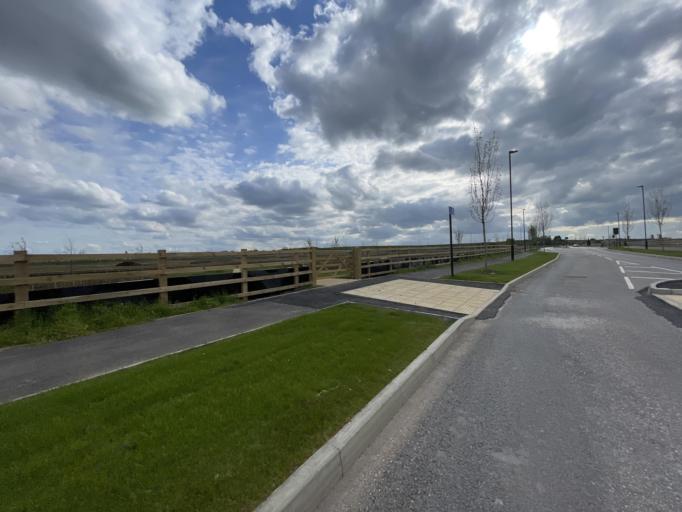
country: GB
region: England
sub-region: Warwickshire
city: Rugby
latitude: 52.3660
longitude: -1.1921
